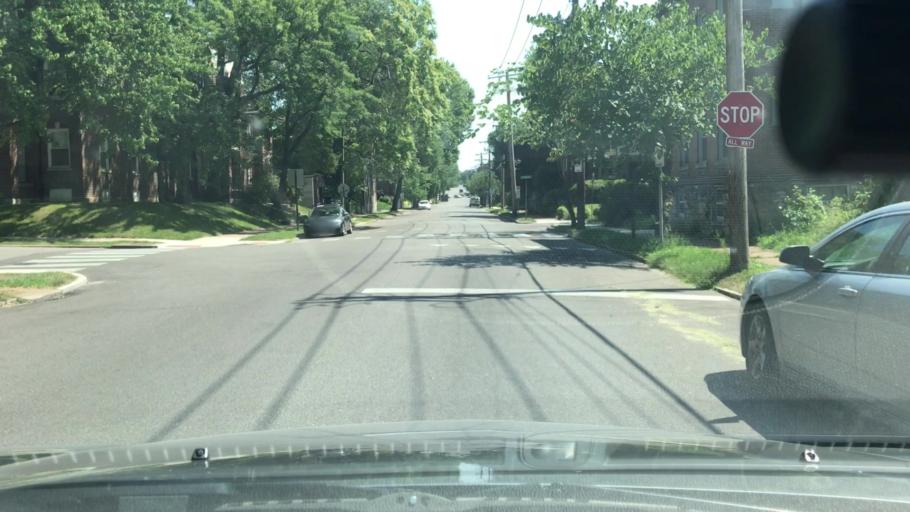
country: US
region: Missouri
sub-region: City of Saint Louis
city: St. Louis
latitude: 38.6019
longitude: -90.2499
